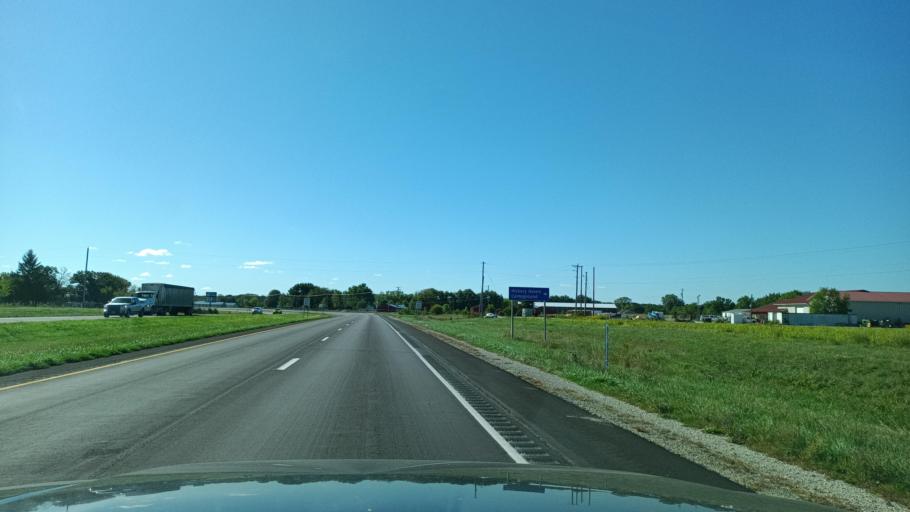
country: US
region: Iowa
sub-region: Lee County
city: Keokuk
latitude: 40.4495
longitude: -91.4423
